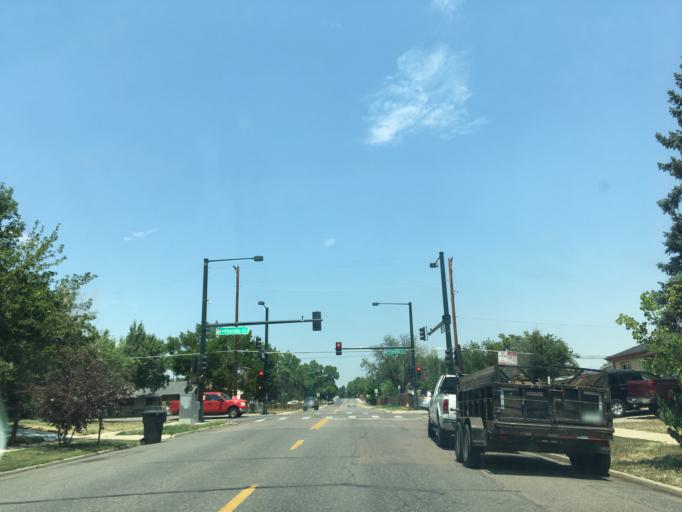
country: US
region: Colorado
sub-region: Arapahoe County
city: Sheridan
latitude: 39.6890
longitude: -105.0343
